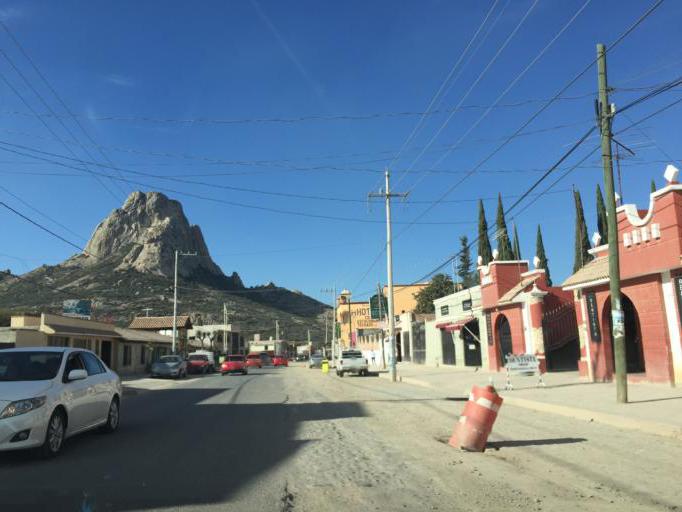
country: MX
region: Queretaro
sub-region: Ezequiel Montes
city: San Jose del Jagueey
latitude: 20.7389
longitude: -99.9386
